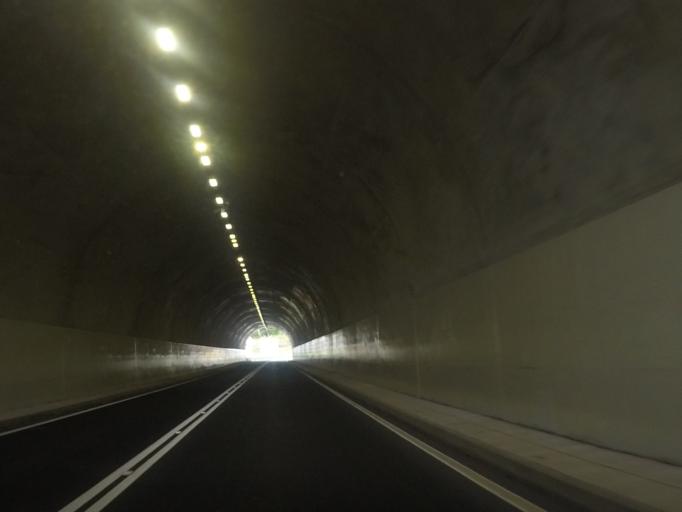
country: PT
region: Madeira
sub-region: Calheta
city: Faja da Ovelha
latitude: 32.7720
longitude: -17.2181
